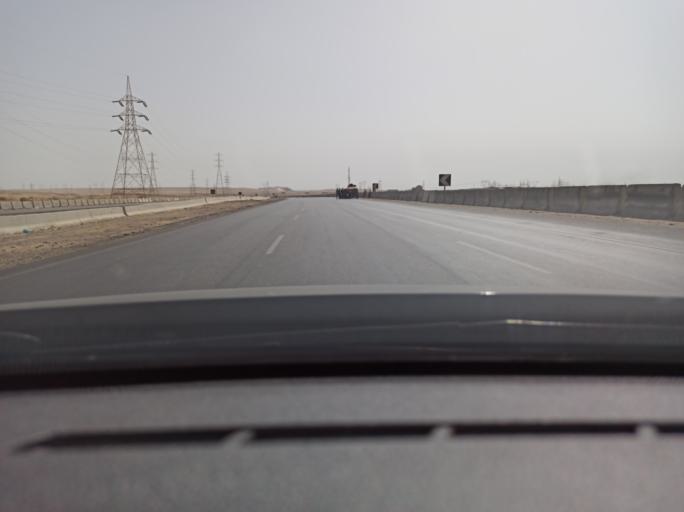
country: EG
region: Muhafazat al Qahirah
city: Halwan
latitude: 29.7677
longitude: 31.3851
